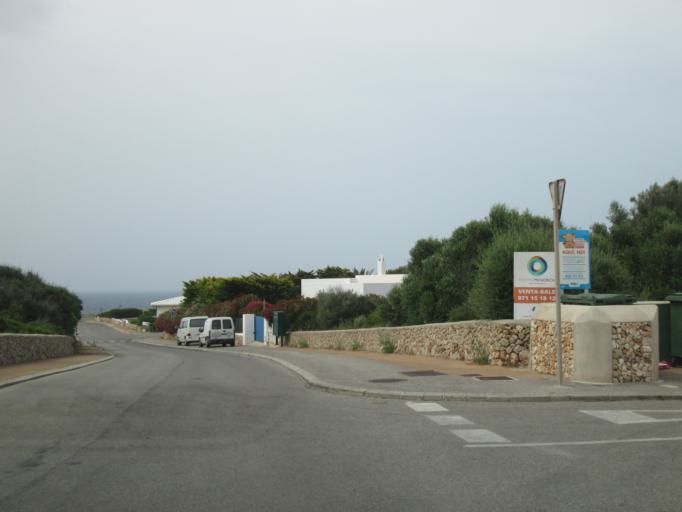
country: ES
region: Balearic Islands
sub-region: Illes Balears
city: Sant Lluis
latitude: 39.8371
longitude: 4.1939
